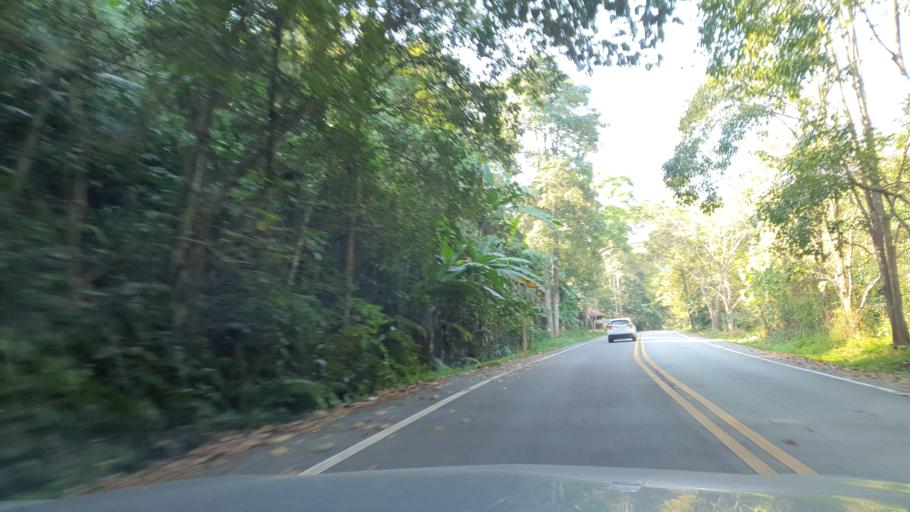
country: TH
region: Chiang Rai
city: Mae Lao
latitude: 19.8730
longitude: 99.6286
